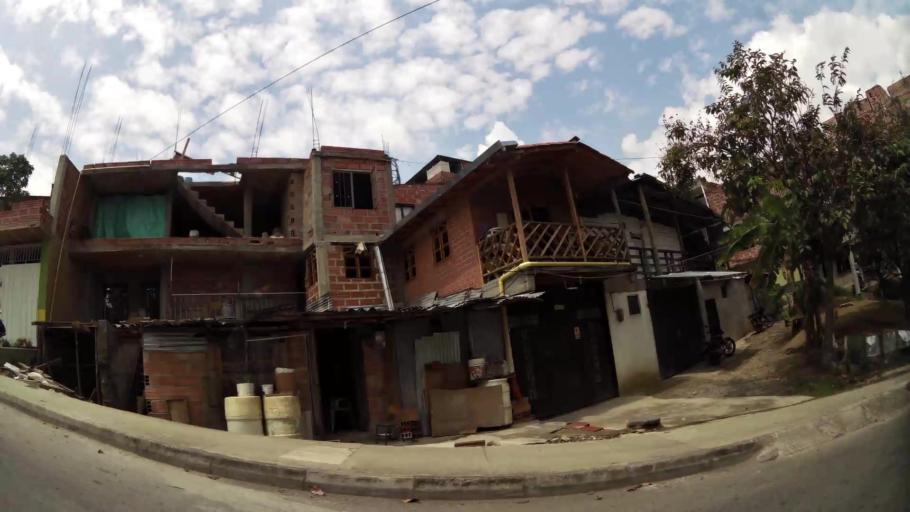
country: CO
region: Antioquia
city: Medellin
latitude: 6.2480
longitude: -75.6198
